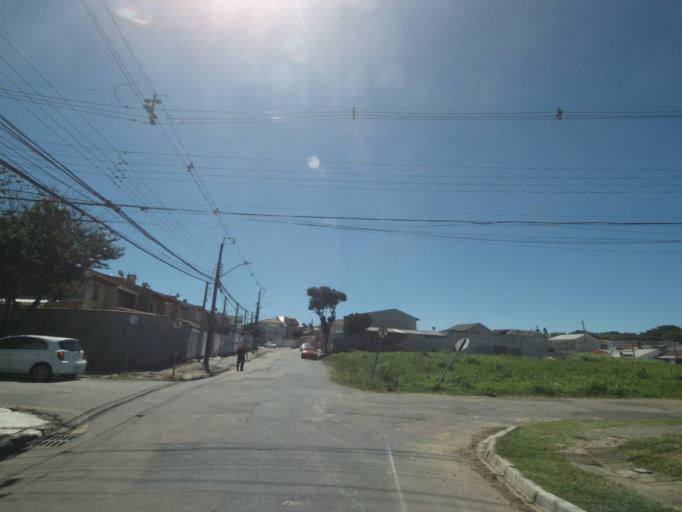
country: BR
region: Parana
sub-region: Curitiba
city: Curitiba
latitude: -25.4711
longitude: -49.3410
